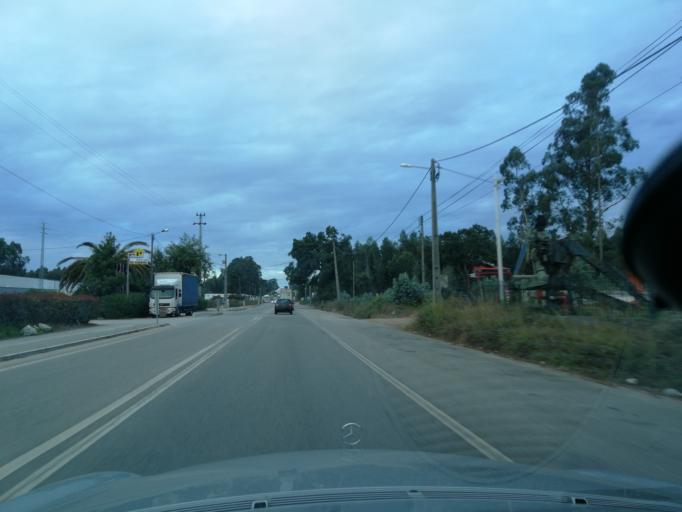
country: PT
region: Aveiro
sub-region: Albergaria-A-Velha
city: Albergaria-a-Velha
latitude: 40.6687
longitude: -8.4747
